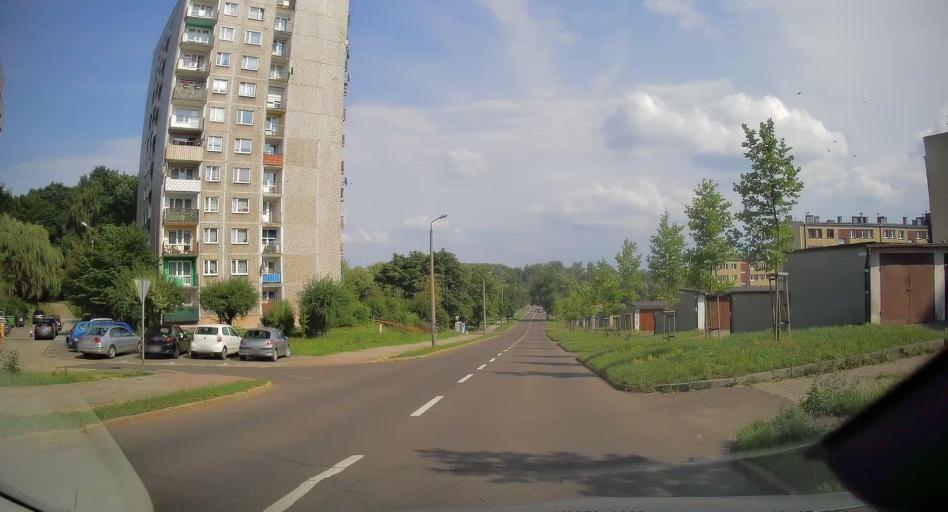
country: PL
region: Silesian Voivodeship
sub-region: Swietochlowice
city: Swietochlowice
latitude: 50.3115
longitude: 18.9167
